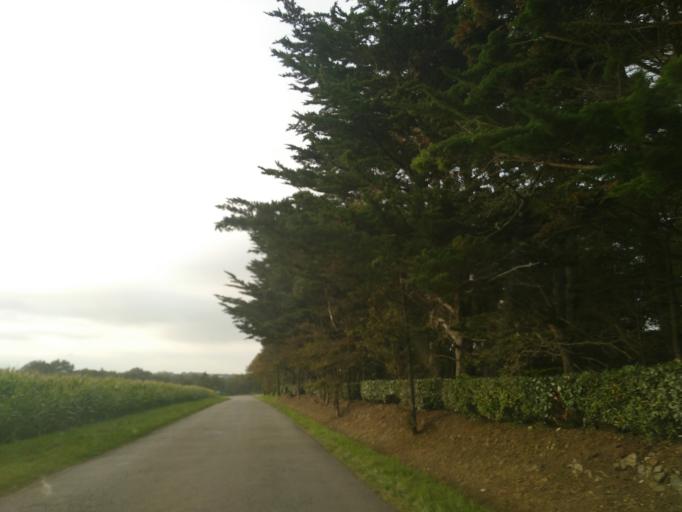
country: FR
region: Brittany
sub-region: Departement du Finistere
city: Crozon
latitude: 48.2388
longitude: -4.4468
